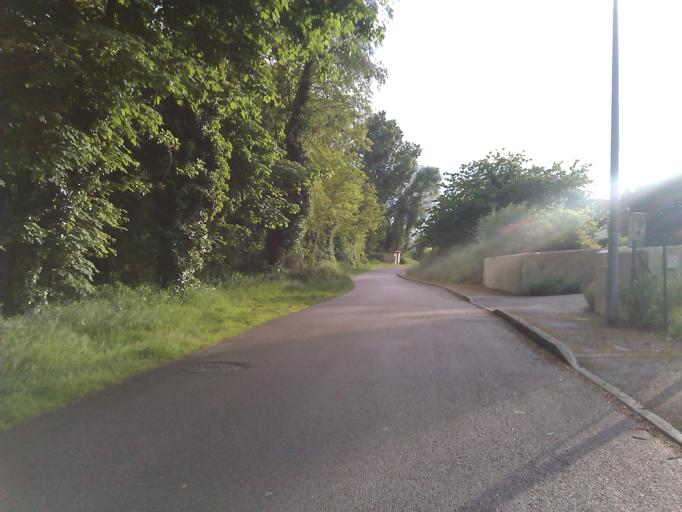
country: FR
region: Bourgogne
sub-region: Departement de Saone-et-Loire
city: Crissey
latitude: 46.8120
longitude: 4.8717
